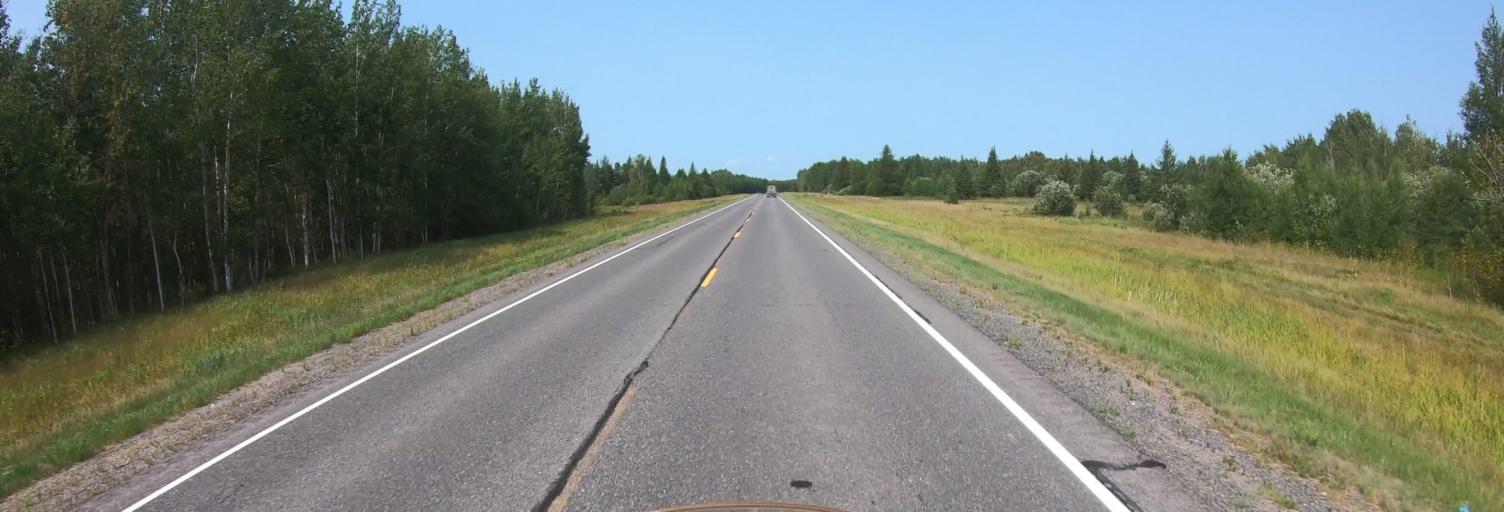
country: US
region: Minnesota
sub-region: Koochiching County
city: International Falls
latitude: 48.5167
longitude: -93.8129
